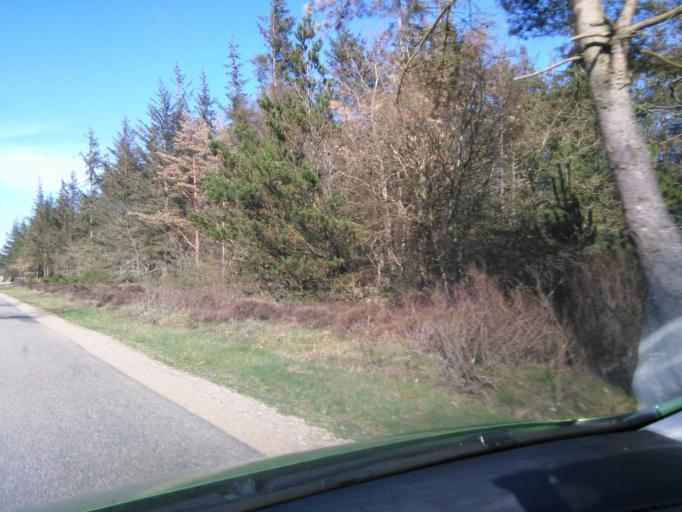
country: DK
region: South Denmark
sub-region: Varde Kommune
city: Oksbol
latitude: 55.7022
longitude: 8.2019
